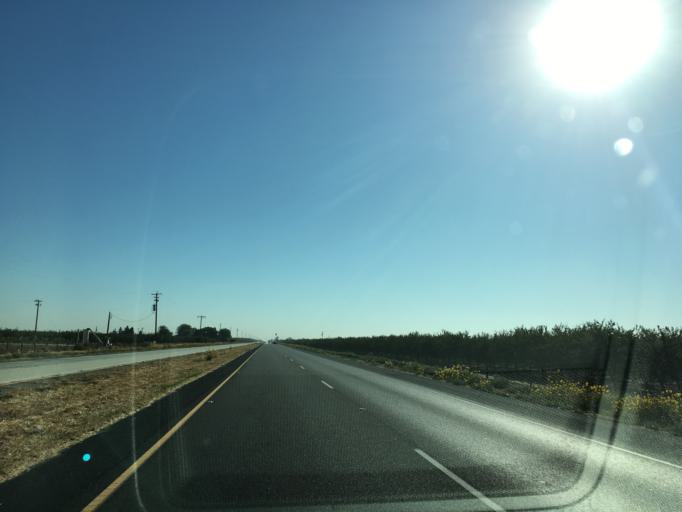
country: US
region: California
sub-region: Merced County
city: Dos Palos
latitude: 37.0835
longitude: -120.4620
